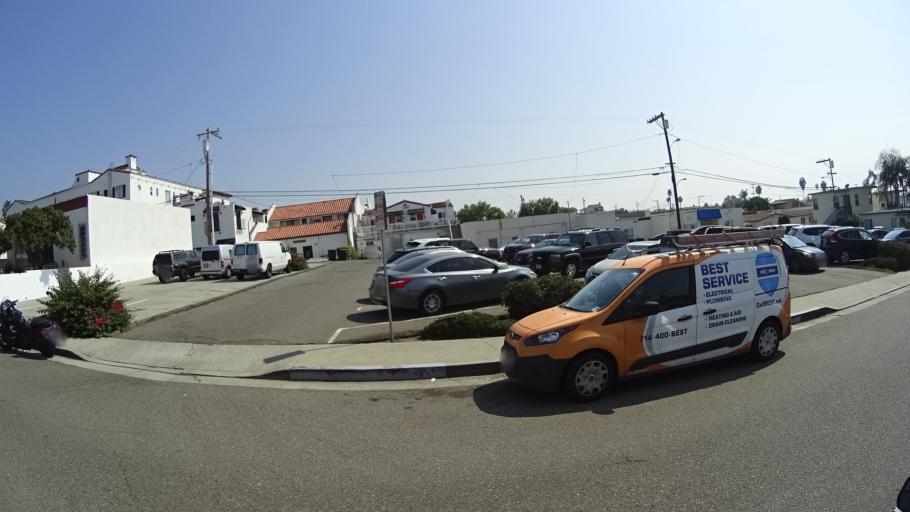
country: US
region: California
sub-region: Orange County
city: San Clemente
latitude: 33.4274
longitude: -117.6145
